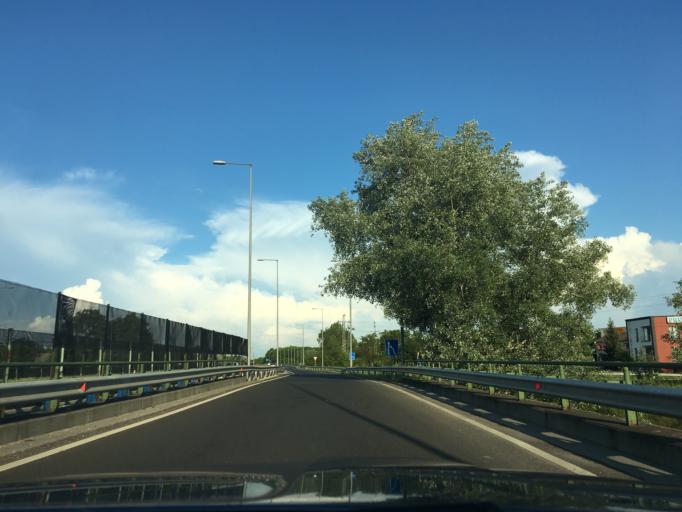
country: HU
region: Pest
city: Toeroekbalint
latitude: 47.4534
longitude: 18.9077
